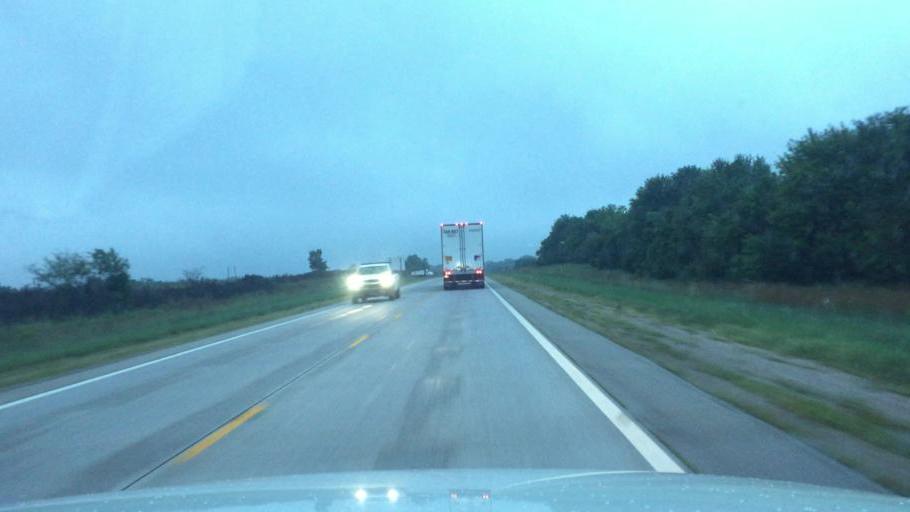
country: US
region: Kansas
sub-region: Neosho County
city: Chanute
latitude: 37.6339
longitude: -95.4796
